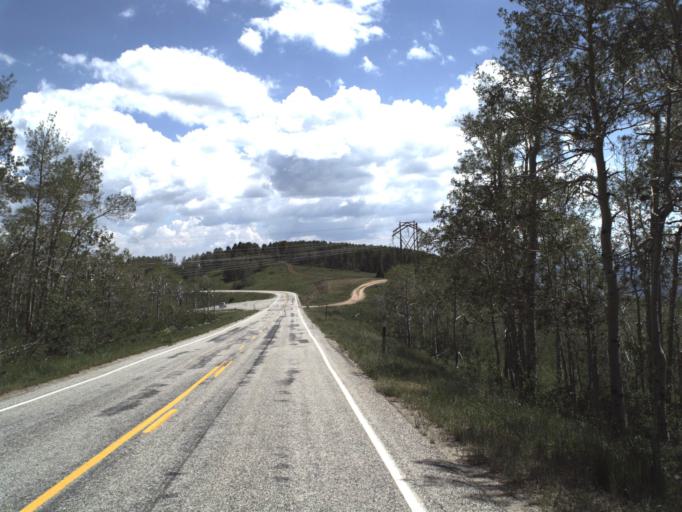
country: US
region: Utah
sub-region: Weber County
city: Wolf Creek
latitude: 41.4168
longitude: -111.5238
